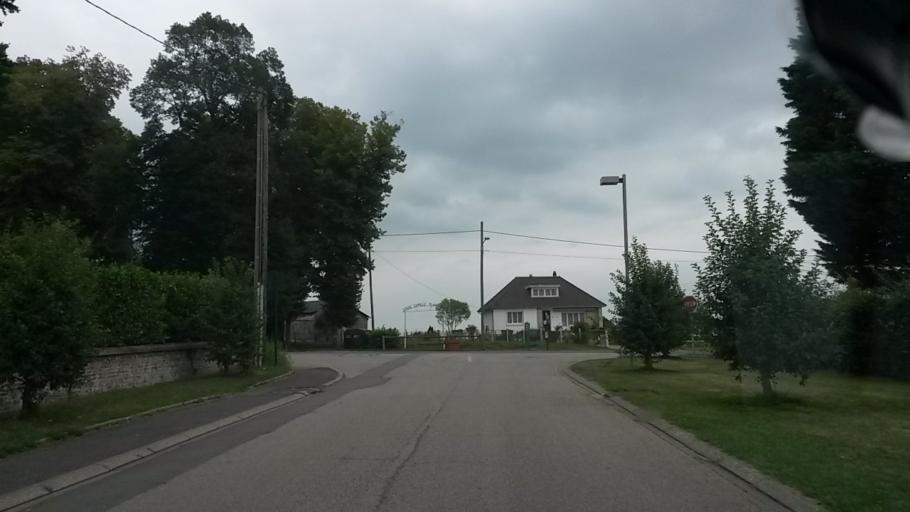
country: FR
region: Haute-Normandie
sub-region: Departement de la Seine-Maritime
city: Forges-les-Eaux
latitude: 49.6054
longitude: 1.5464
